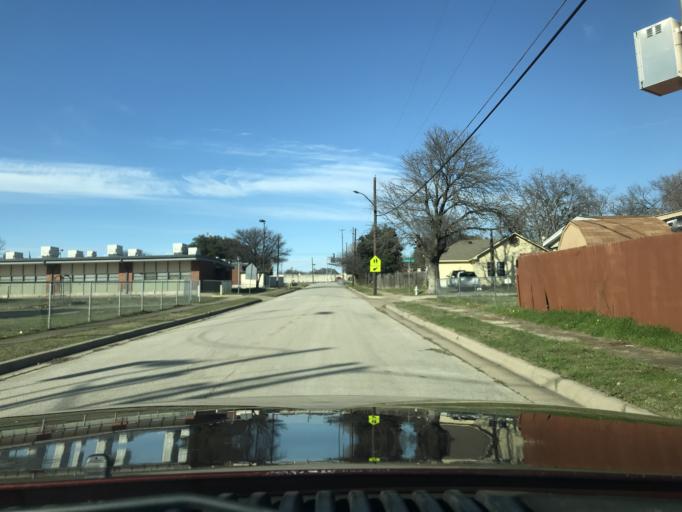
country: US
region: Texas
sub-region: Tarrant County
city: Edgecliff Village
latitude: 32.6628
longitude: -97.3437
